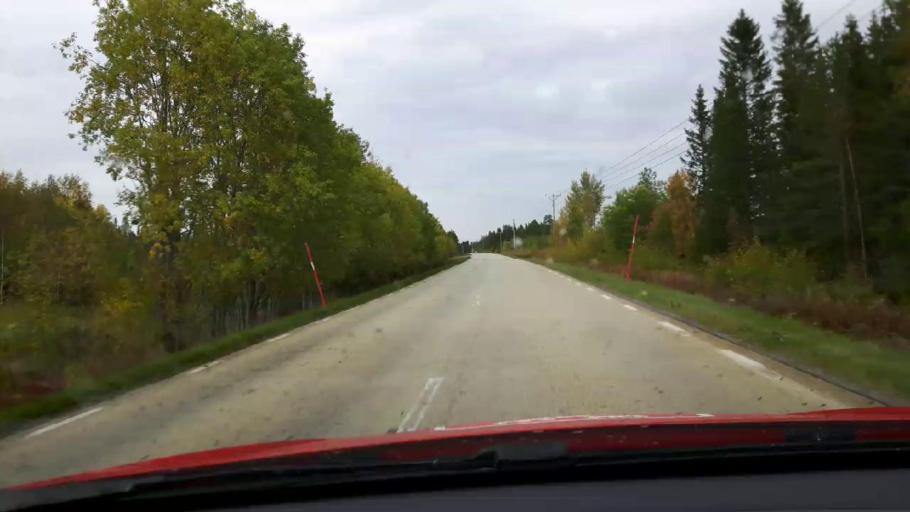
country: SE
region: Jaemtland
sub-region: Bergs Kommun
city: Hoverberg
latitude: 62.9622
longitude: 14.3473
